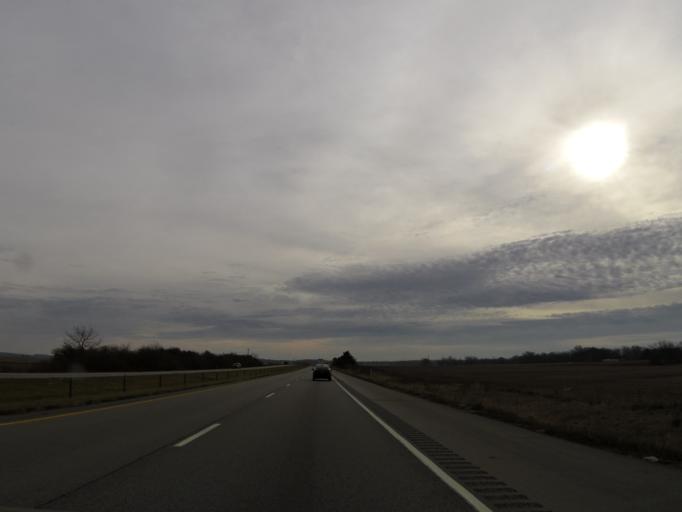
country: US
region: Indiana
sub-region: Montgomery County
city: Crawfordsville
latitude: 40.0686
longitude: -86.8562
